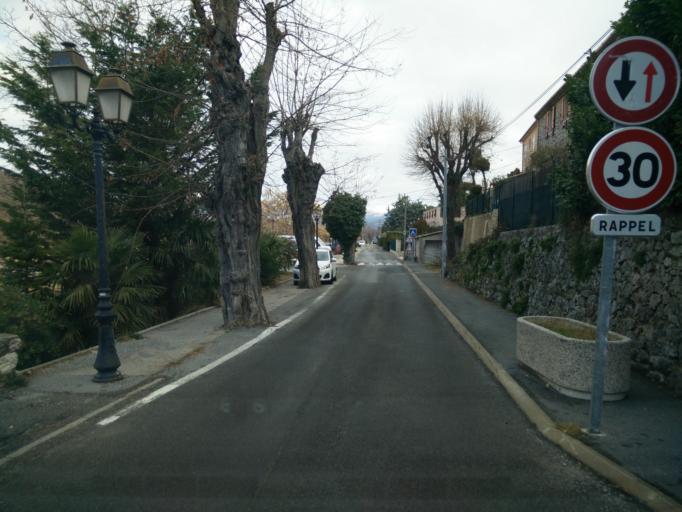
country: FR
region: Provence-Alpes-Cote d'Azur
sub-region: Departement des Alpes-Maritimes
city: Gilette
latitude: 43.8259
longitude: 7.1238
